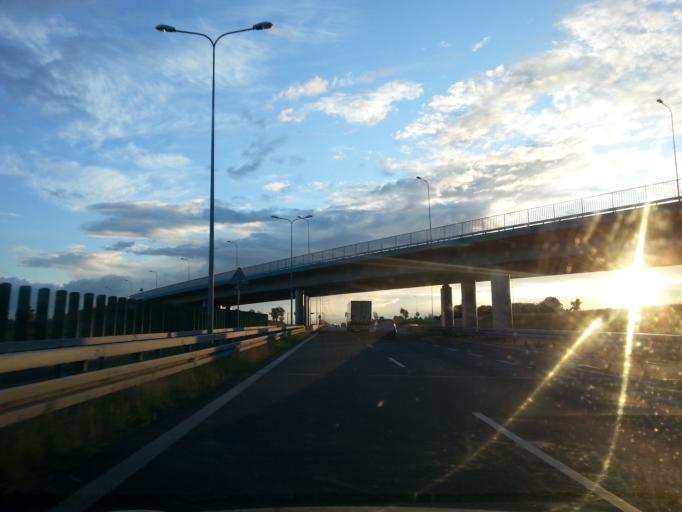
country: PL
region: Lower Silesian Voivodeship
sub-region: Powiat olesnicki
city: Sycow
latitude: 51.2955
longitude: 17.6809
